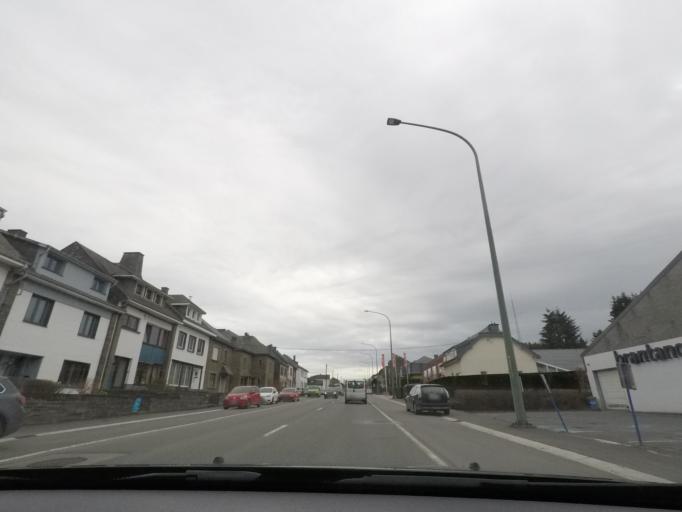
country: BE
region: Wallonia
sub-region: Province du Luxembourg
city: Bastogne
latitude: 49.9969
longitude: 5.7197
